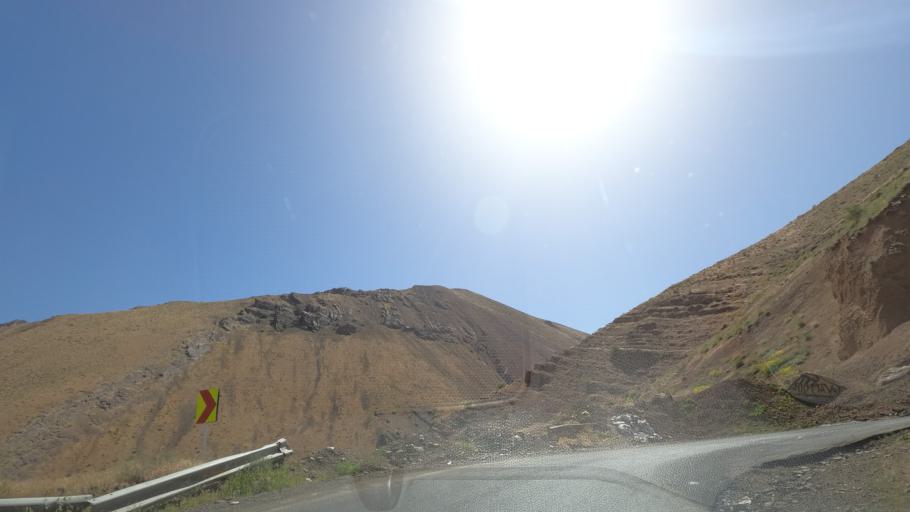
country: IR
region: Alborz
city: Karaj
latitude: 35.9406
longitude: 51.0866
